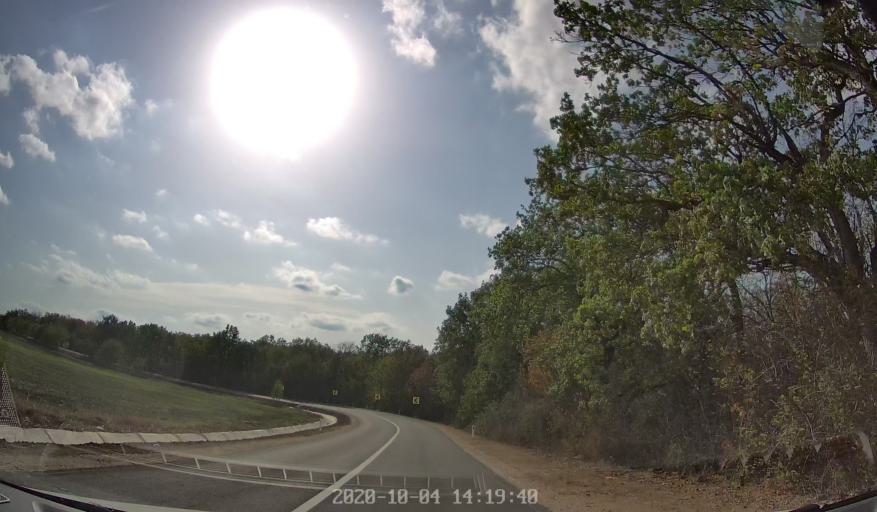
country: MD
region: Rezina
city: Saharna
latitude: 47.5894
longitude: 28.9711
